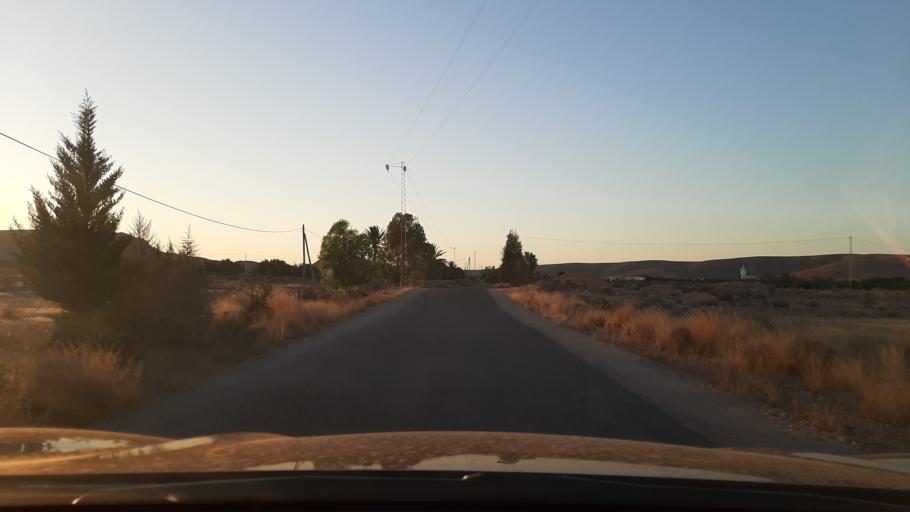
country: TN
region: Qabis
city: Matmata
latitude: 33.5639
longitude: 10.1799
